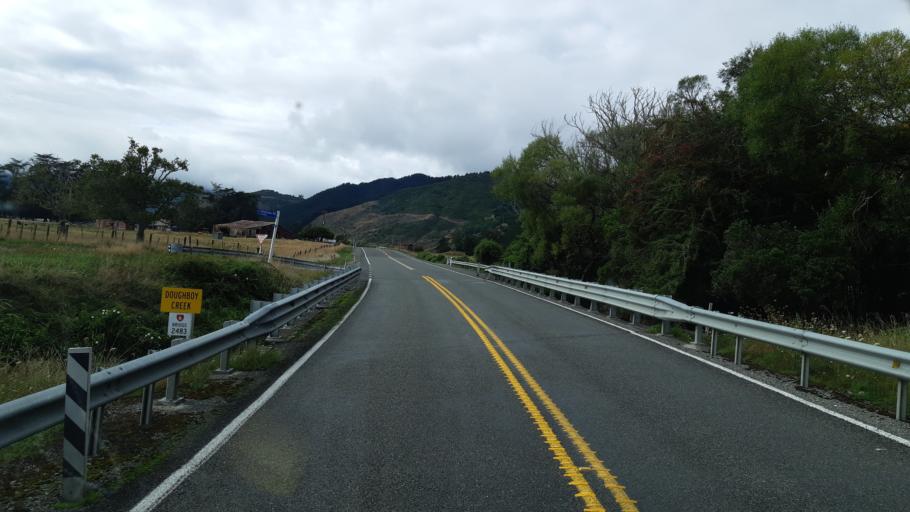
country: NZ
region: West Coast
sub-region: Buller District
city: Westport
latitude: -41.7836
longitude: 172.2759
